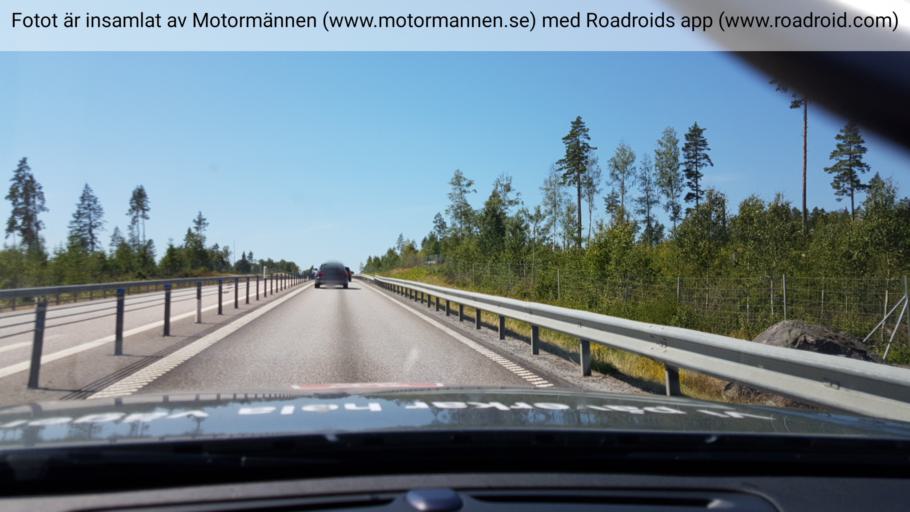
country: SE
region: OErebro
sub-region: Laxa Kommun
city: Laxa
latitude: 58.9752
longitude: 14.5628
